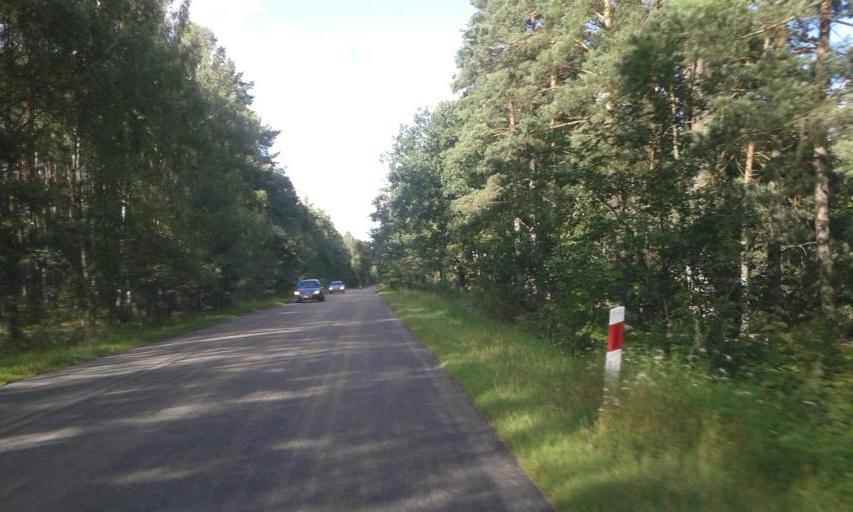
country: PL
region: West Pomeranian Voivodeship
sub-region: Powiat szczecinecki
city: Barwice
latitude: 53.6651
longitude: 16.3367
